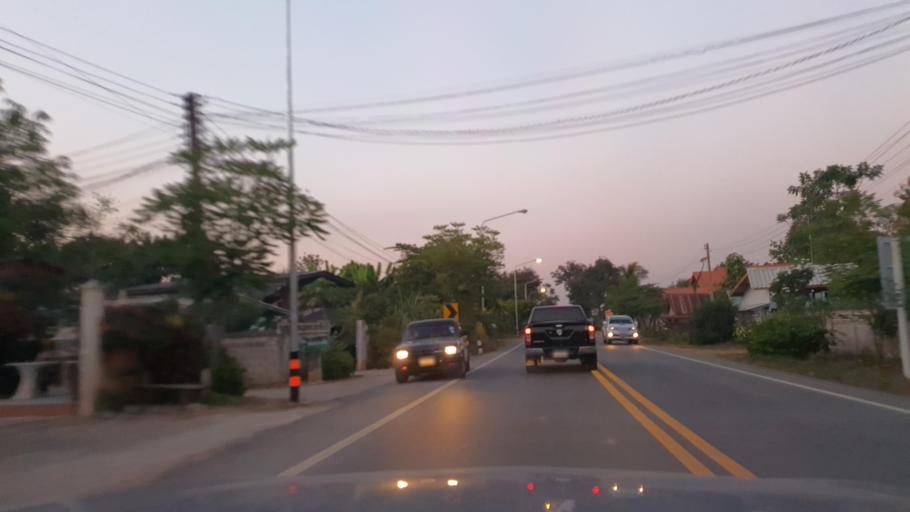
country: TH
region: Phayao
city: Dok Kham Tai
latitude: 19.1456
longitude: 100.0138
